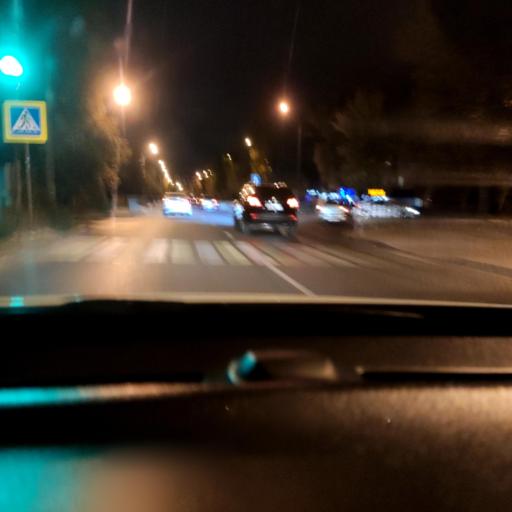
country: RU
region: Voronezj
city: Voronezh
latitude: 51.7044
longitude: 39.2292
